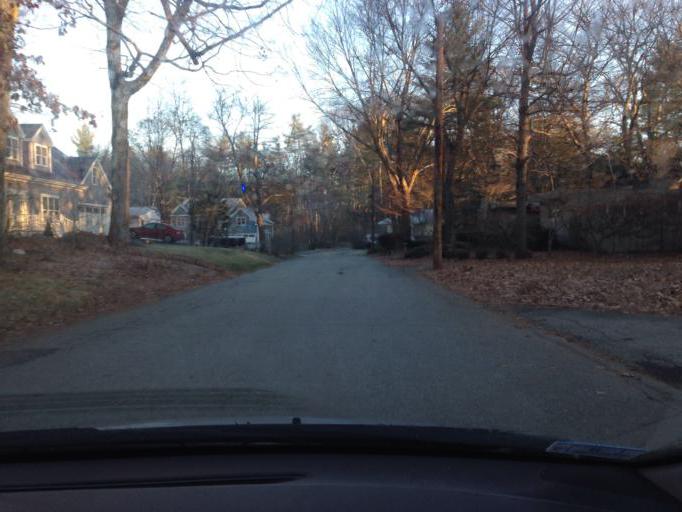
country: US
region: Massachusetts
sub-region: Middlesex County
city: Bedford
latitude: 42.4970
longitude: -71.2793
